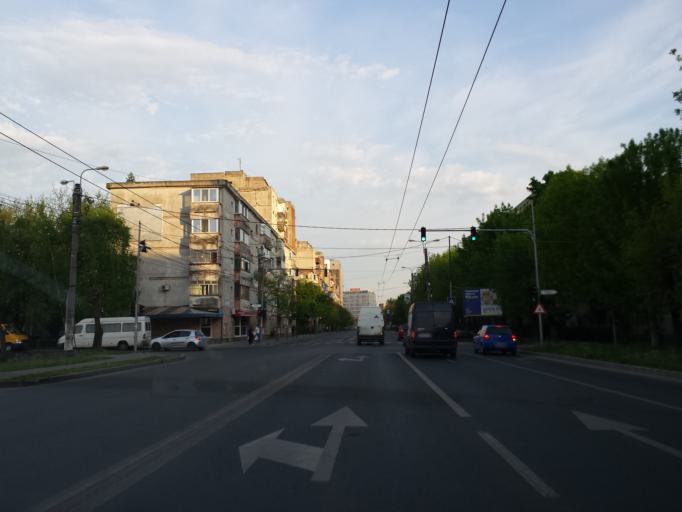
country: RO
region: Timis
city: Timisoara
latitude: 45.7677
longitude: 21.2215
